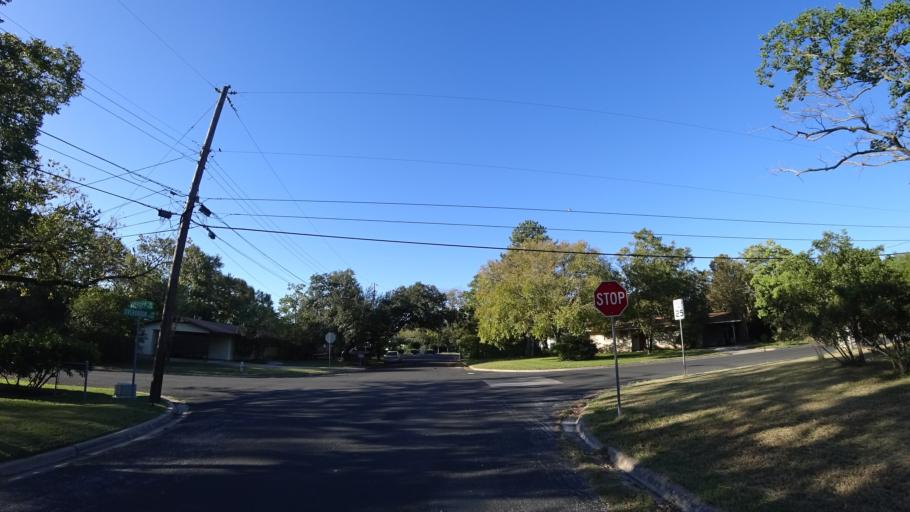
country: US
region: Texas
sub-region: Travis County
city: Austin
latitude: 30.3025
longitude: -97.6820
